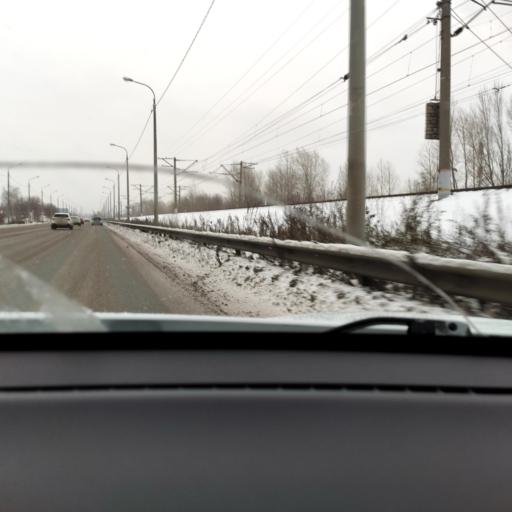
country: RU
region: Tatarstan
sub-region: Gorod Kazan'
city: Kazan
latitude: 55.8458
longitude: 49.1090
